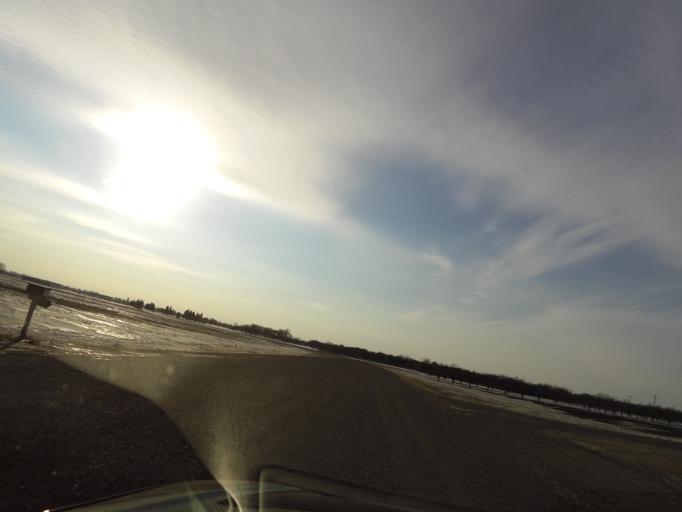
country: US
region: North Dakota
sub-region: Walsh County
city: Grafton
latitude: 48.4198
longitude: -97.3767
